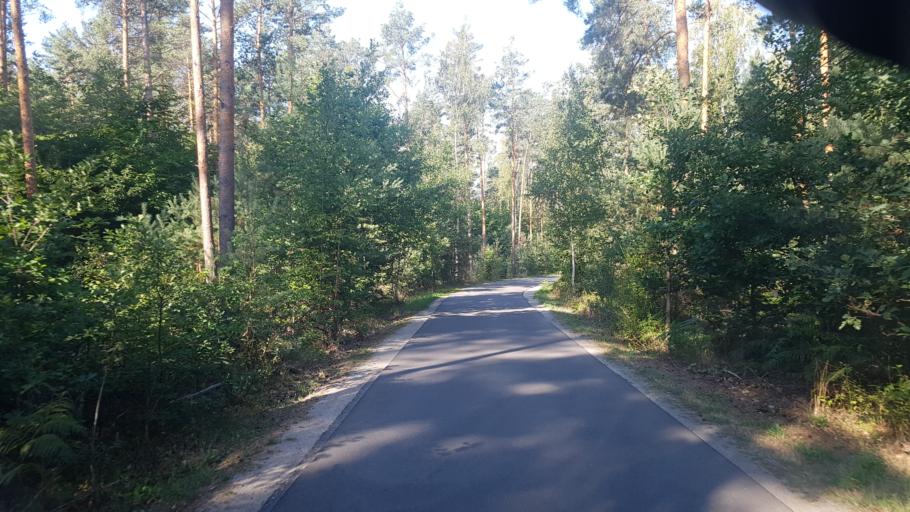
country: DE
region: Brandenburg
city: Plessa
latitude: 51.5268
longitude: 13.6593
